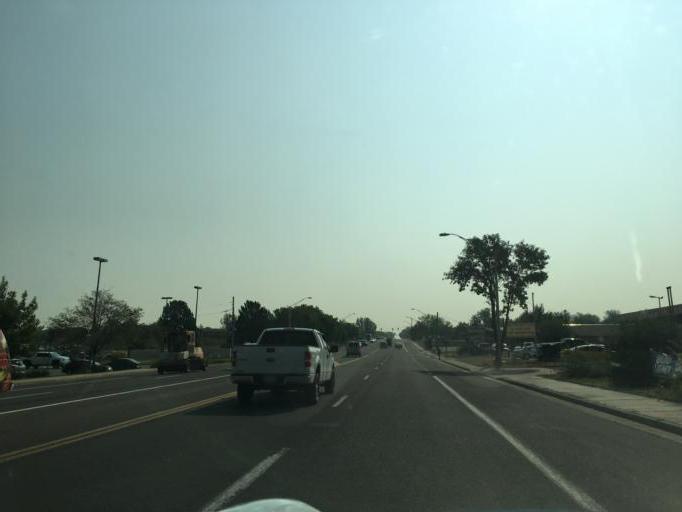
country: US
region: Colorado
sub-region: Adams County
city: Brighton
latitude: 39.9868
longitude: -104.8008
